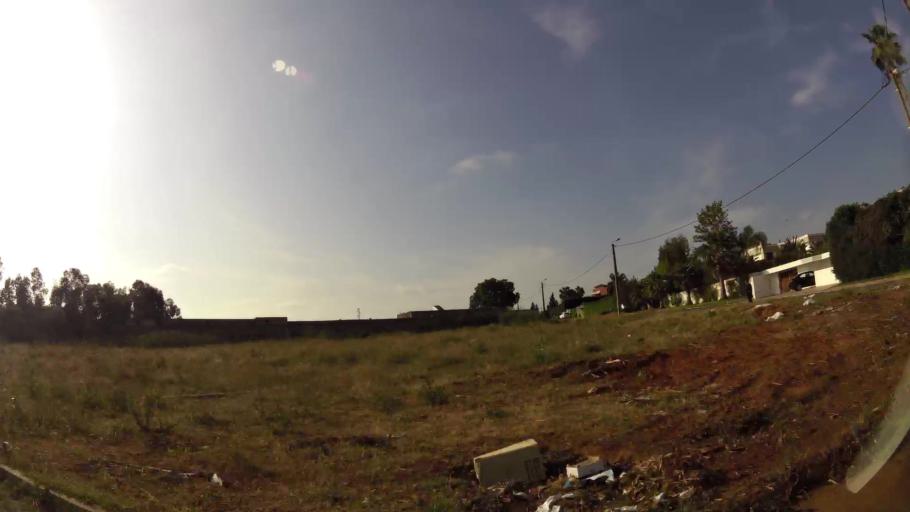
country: MA
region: Rabat-Sale-Zemmour-Zaer
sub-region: Rabat
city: Rabat
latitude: 33.9352
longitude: -6.8084
